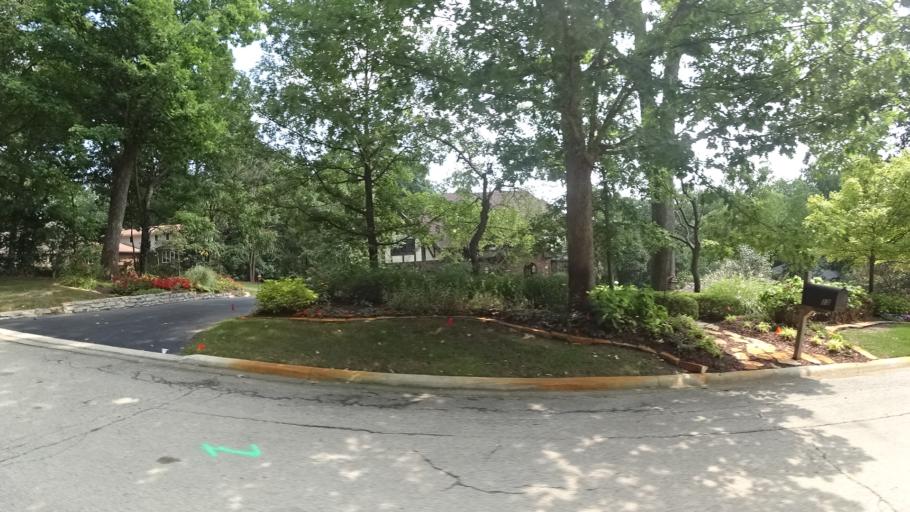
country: US
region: Illinois
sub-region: Cook County
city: Orland Park
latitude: 41.6321
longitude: -87.8792
